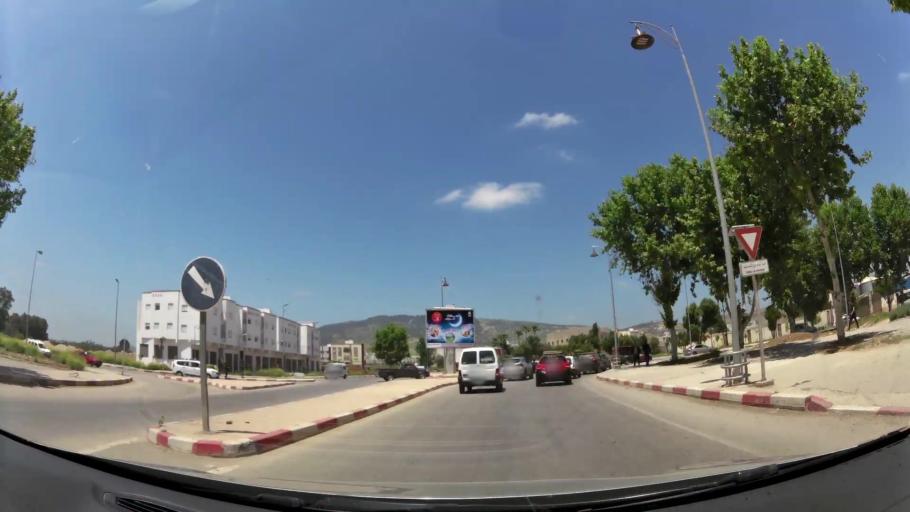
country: MA
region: Fes-Boulemane
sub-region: Fes
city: Fes
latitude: 34.0396
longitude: -5.0342
